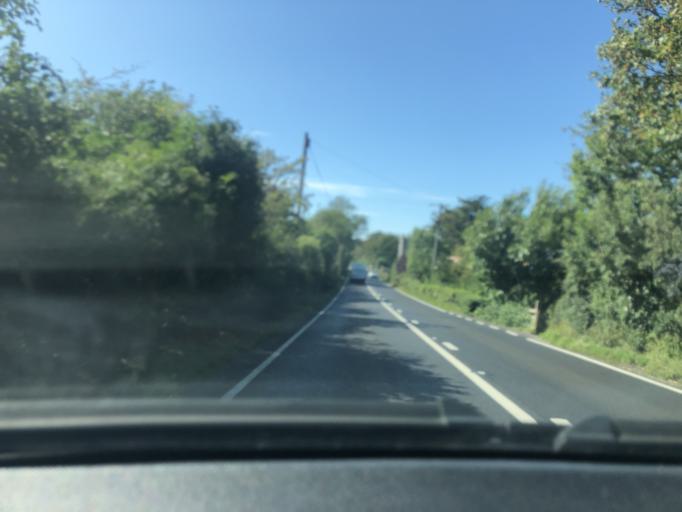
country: GB
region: England
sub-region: Somerset
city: Woolavington
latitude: 51.1455
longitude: -2.8947
